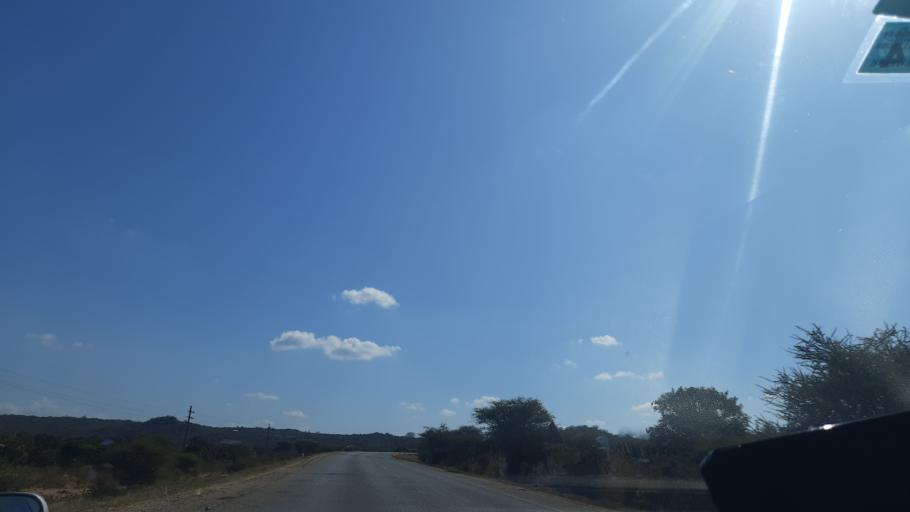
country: TZ
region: Singida
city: Kilimatinde
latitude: -5.7824
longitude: 34.8900
